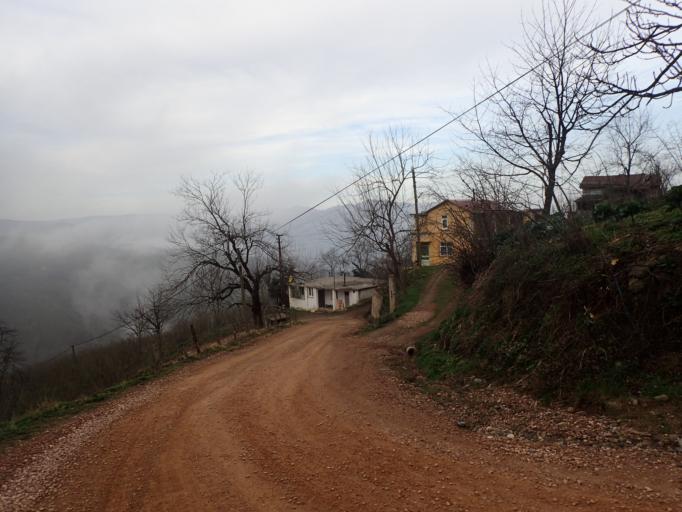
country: TR
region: Ordu
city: Camas
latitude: 40.8902
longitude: 37.5144
